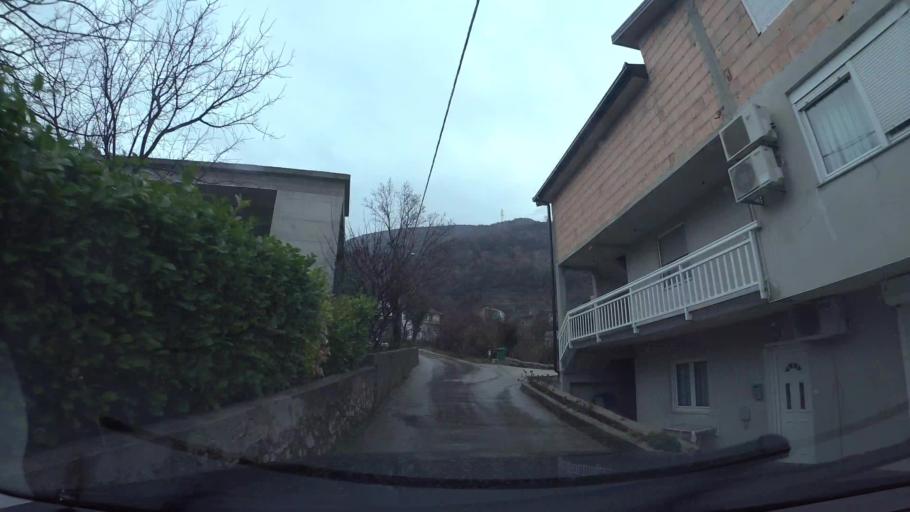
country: BA
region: Federation of Bosnia and Herzegovina
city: Cim
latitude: 43.3546
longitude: 17.7825
